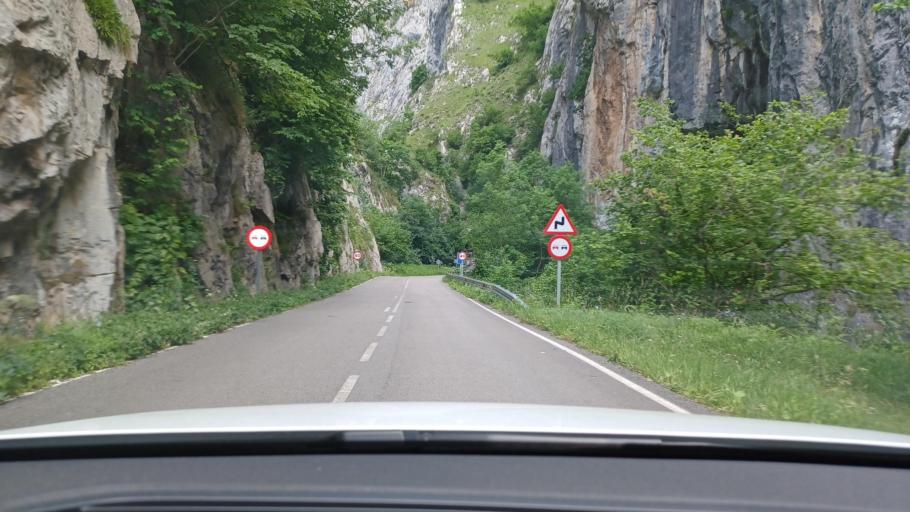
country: ES
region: Asturias
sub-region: Province of Asturias
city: La Plaza
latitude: 43.1178
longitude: -6.0507
